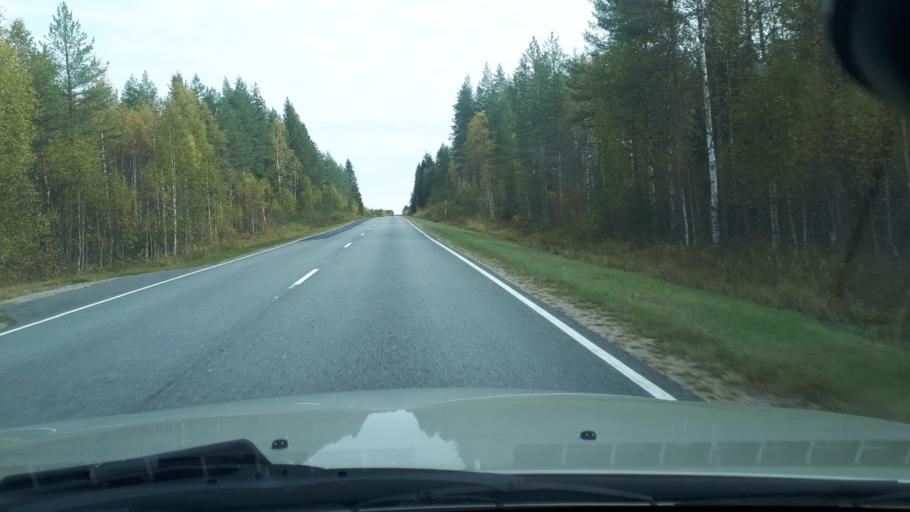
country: FI
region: Lapland
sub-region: Rovaniemi
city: Ranua
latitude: 65.9660
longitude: 26.0851
